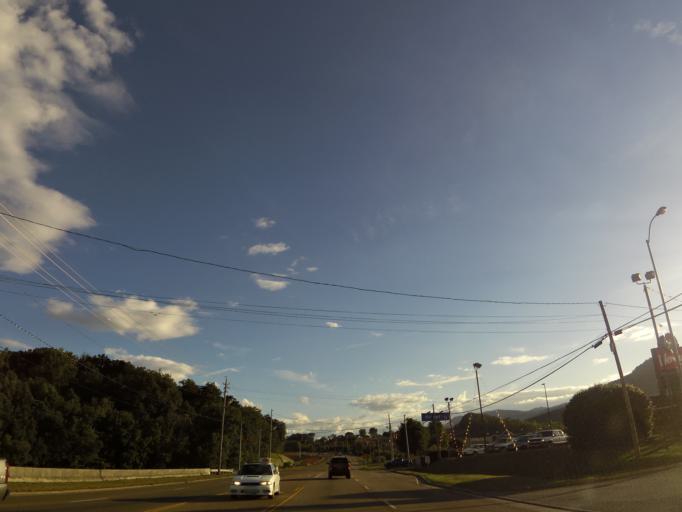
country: US
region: Tennessee
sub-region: Cocke County
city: Newport
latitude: 35.9438
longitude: -83.2079
